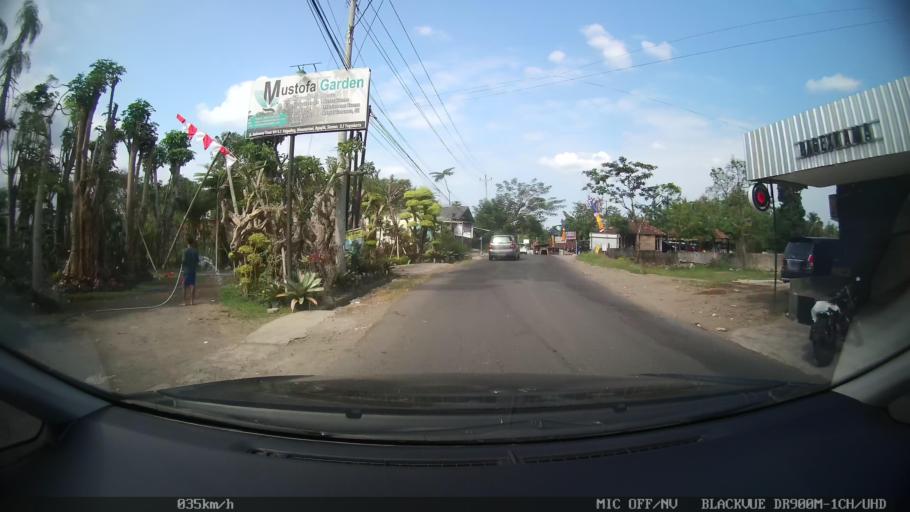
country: ID
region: Daerah Istimewa Yogyakarta
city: Depok
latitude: -7.7287
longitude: 110.4099
